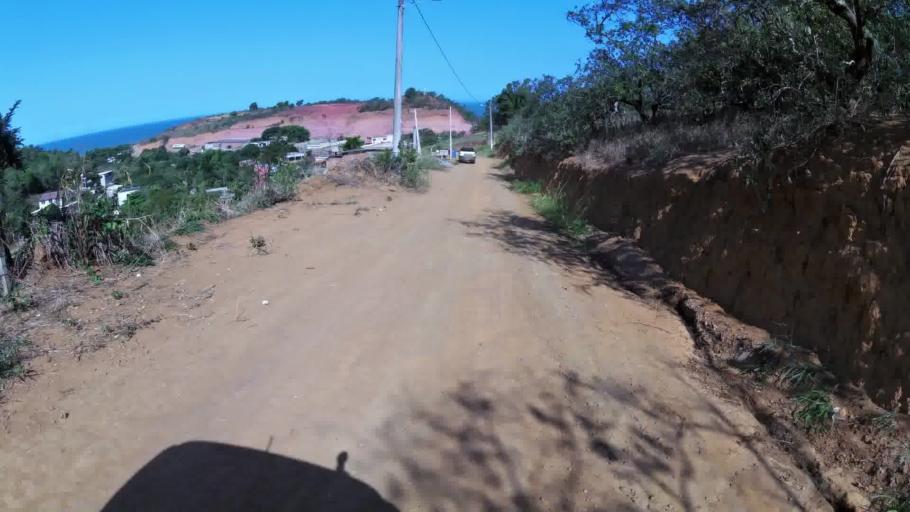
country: BR
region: Espirito Santo
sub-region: Piuma
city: Piuma
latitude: -20.8866
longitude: -40.7723
